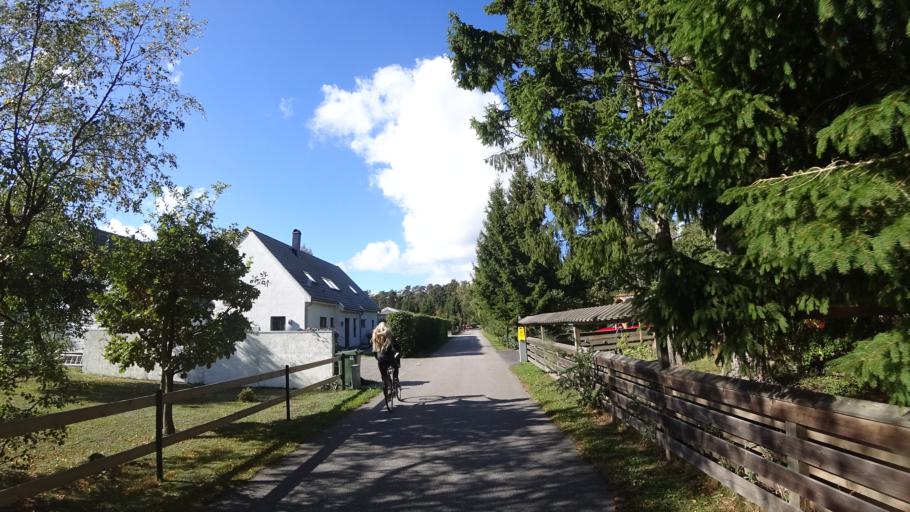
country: SE
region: Skane
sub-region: Kavlinge Kommun
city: Loddekopinge
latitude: 55.7556
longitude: 12.9900
